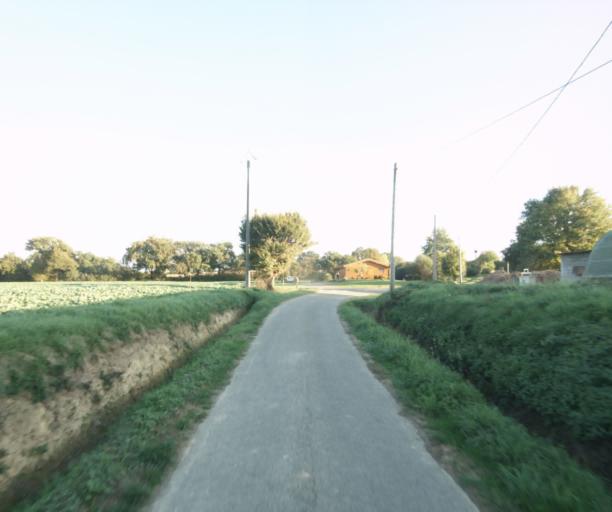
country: FR
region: Midi-Pyrenees
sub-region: Departement du Gers
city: Eauze
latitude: 43.7440
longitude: 0.1661
